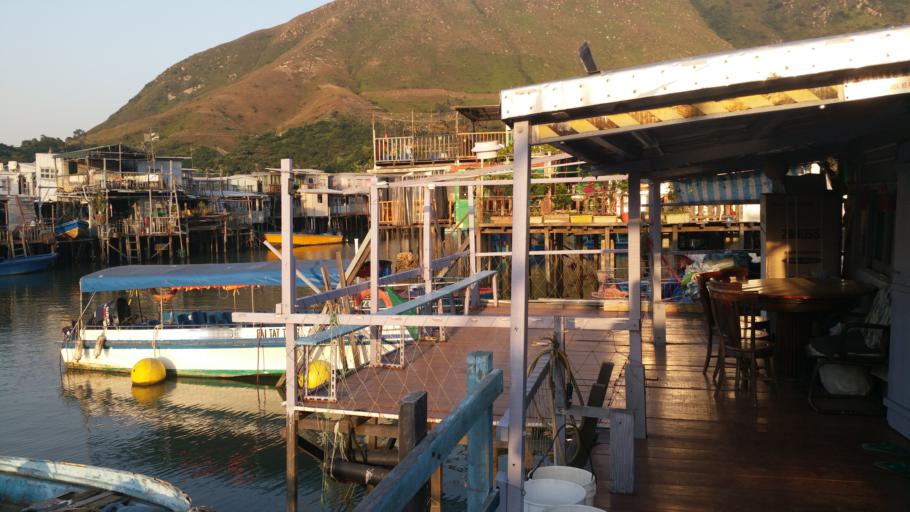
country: HK
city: Tai O
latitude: 22.2551
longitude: 113.8639
